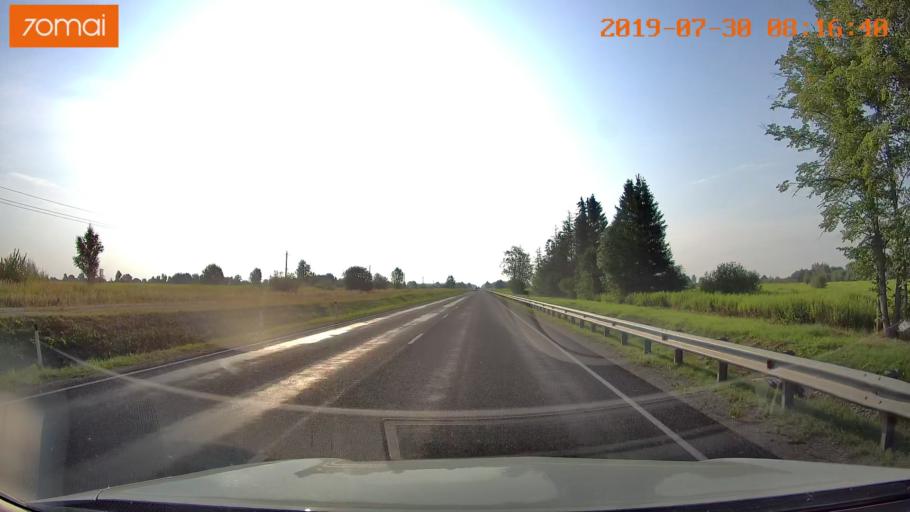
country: RU
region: Kaliningrad
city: Zheleznodorozhnyy
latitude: 54.6394
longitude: 21.4168
